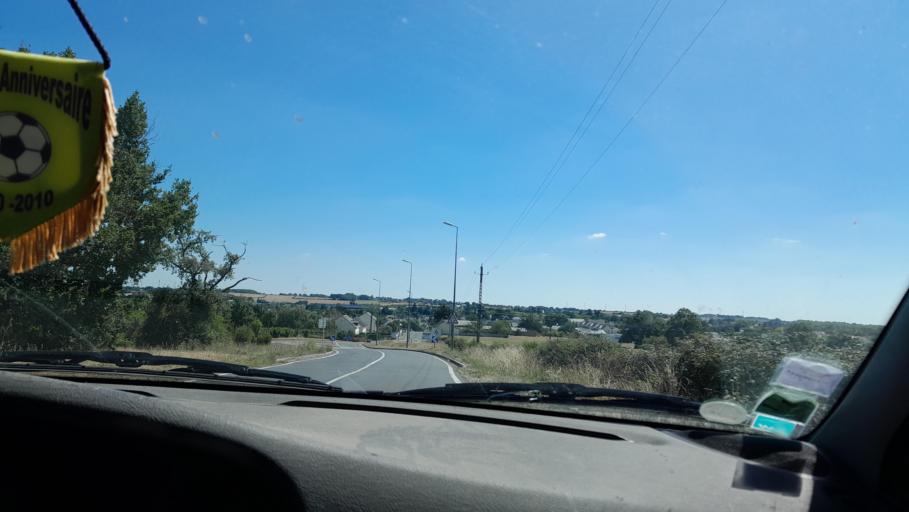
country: FR
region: Pays de la Loire
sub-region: Departement de la Loire-Atlantique
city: Saint-Mars-la-Jaille
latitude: 47.5347
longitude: -1.1866
